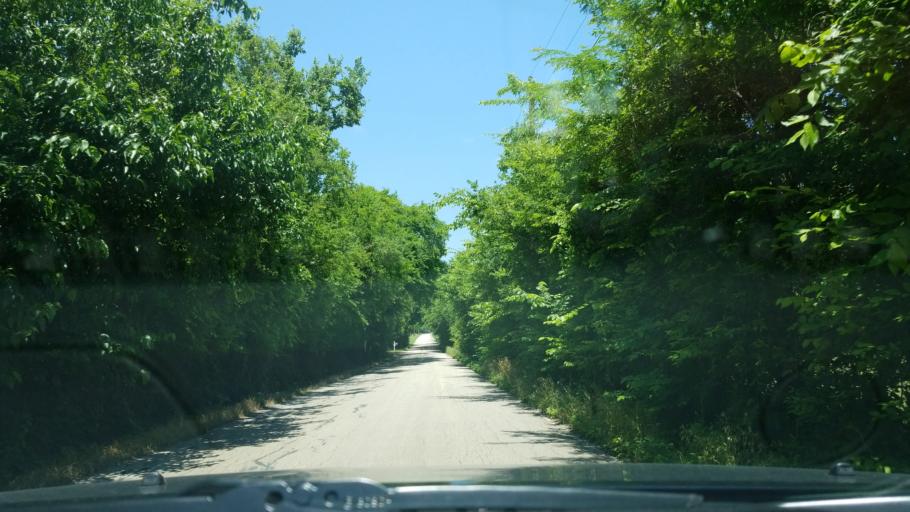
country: US
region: Texas
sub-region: Denton County
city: Sanger
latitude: 33.3525
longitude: -97.1960
